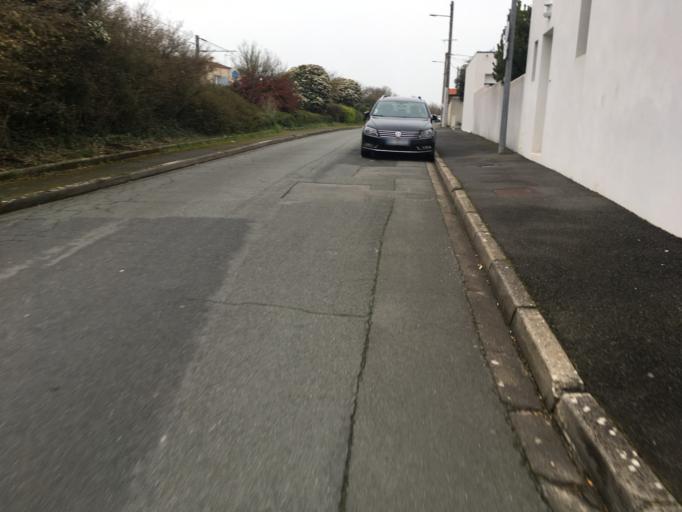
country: FR
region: Poitou-Charentes
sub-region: Departement de la Charente-Maritime
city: La Rochelle
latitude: 46.1624
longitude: -1.1734
